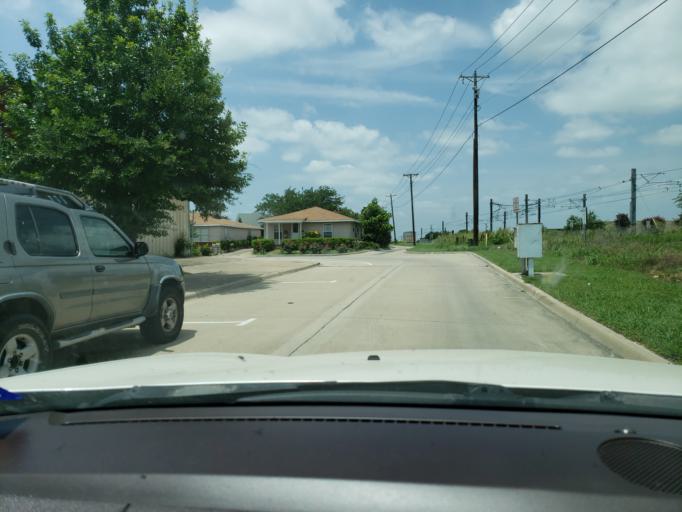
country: US
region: Texas
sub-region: Dallas County
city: Rowlett
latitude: 32.9035
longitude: -96.5661
